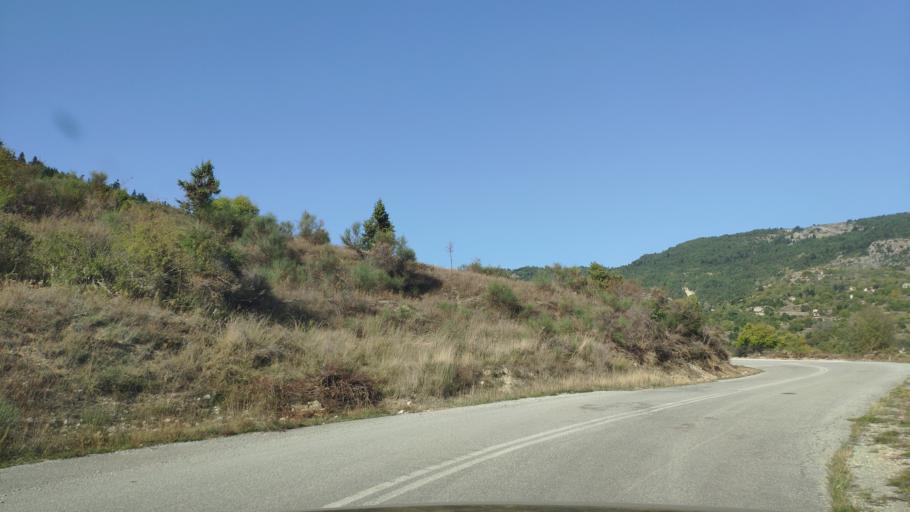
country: GR
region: West Greece
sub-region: Nomos Achaias
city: Aiyira
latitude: 38.0088
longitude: 22.4008
